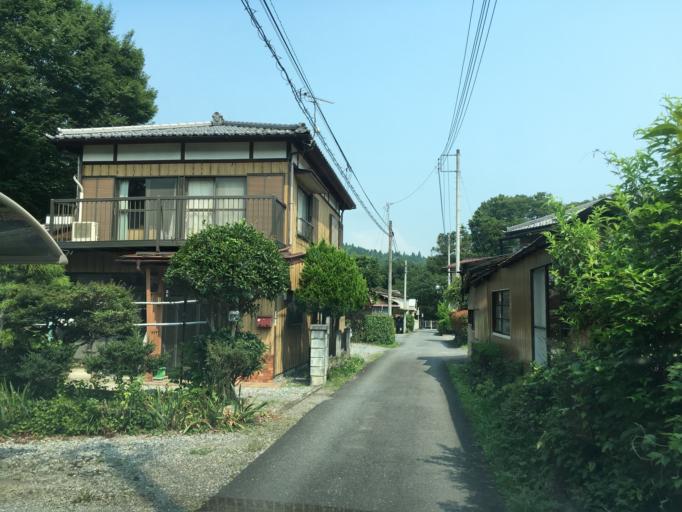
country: JP
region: Saitama
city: Chichibu
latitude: 36.0083
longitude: 139.1096
